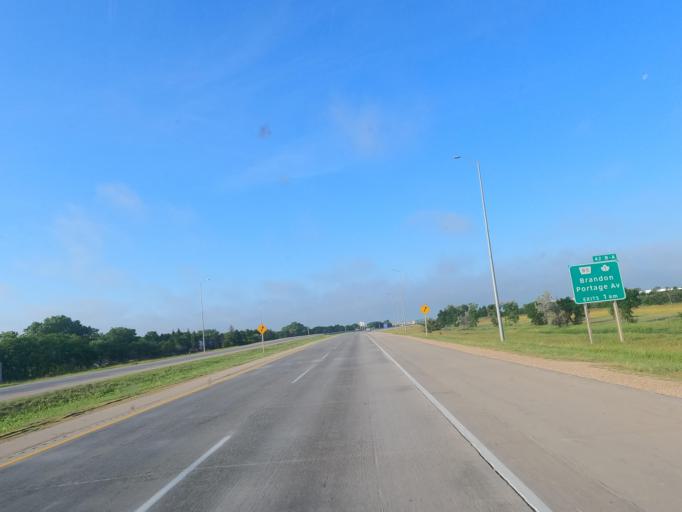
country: CA
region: Manitoba
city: Headingley
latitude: 49.8906
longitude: -97.3222
